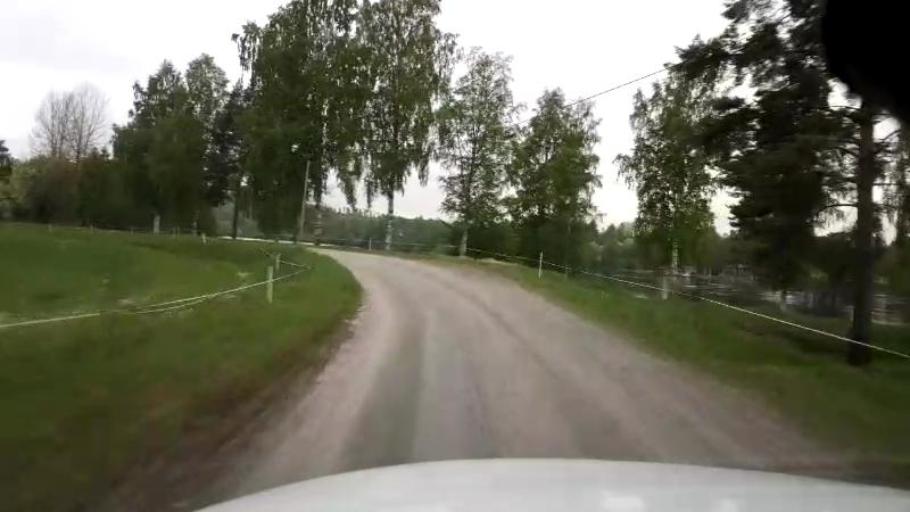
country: SE
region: Gaevleborg
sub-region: Ljusdals Kommun
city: Jaervsoe
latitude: 61.7587
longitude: 16.1686
